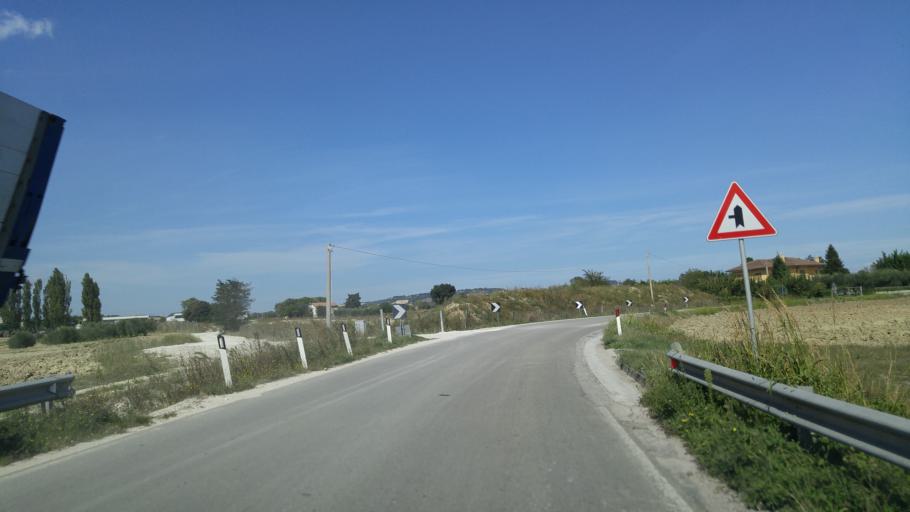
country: IT
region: The Marches
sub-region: Provincia di Pesaro e Urbino
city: Lucrezia
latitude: 43.7645
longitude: 12.9673
